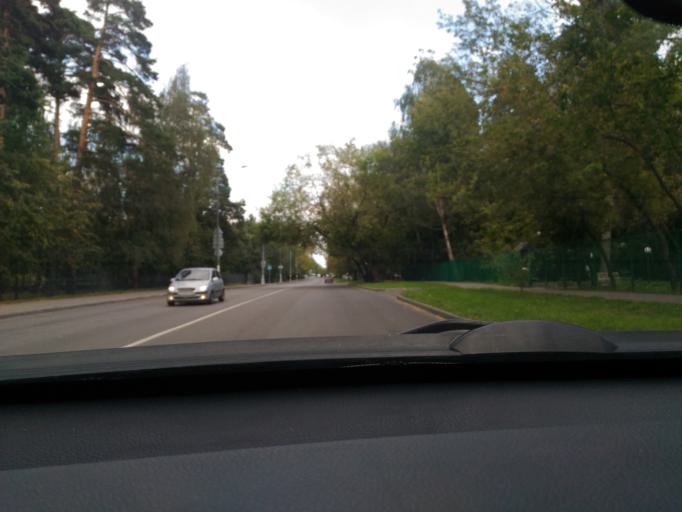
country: RU
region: Moscow
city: Vatutino
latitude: 55.8873
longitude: 37.6947
